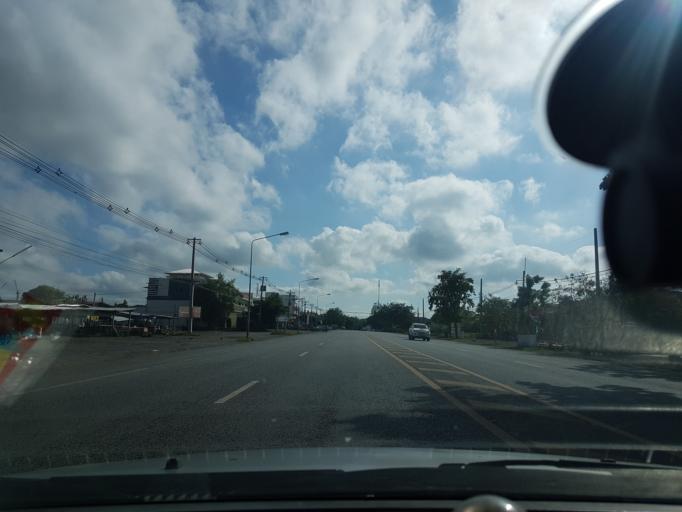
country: TH
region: Lop Buri
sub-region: Amphoe Tha Luang
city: Tha Luang
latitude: 15.0795
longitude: 101.0452
